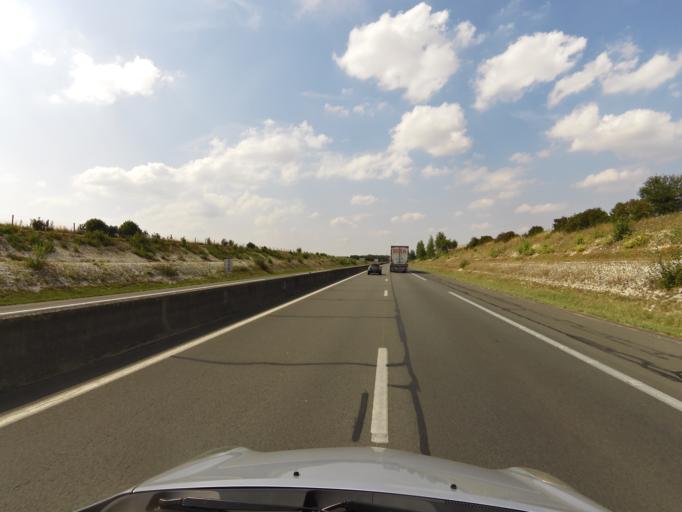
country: FR
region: Picardie
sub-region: Departement de l'Aisne
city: Aulnois-sous-Laon
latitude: 49.6265
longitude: 3.6252
